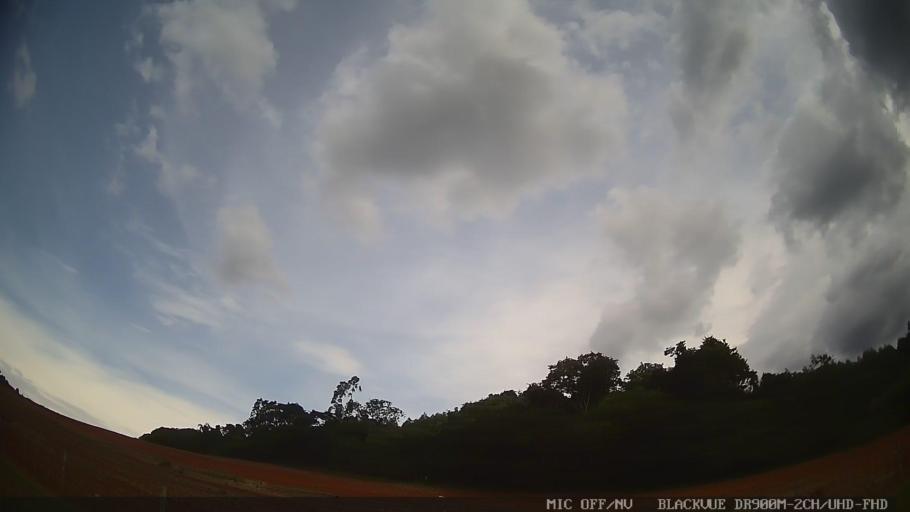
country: BR
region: Sao Paulo
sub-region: Amparo
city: Amparo
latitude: -22.8149
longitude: -46.7553
